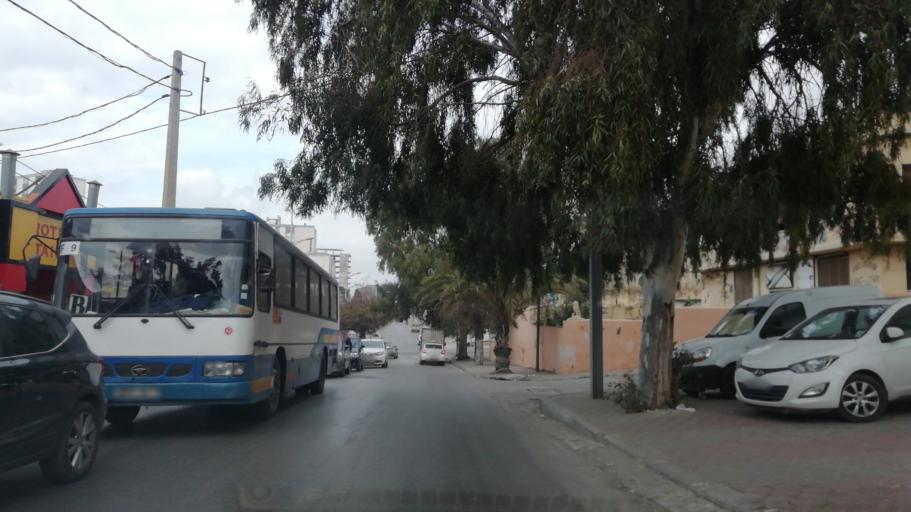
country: DZ
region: Oran
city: Oran
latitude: 35.7045
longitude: -0.6104
